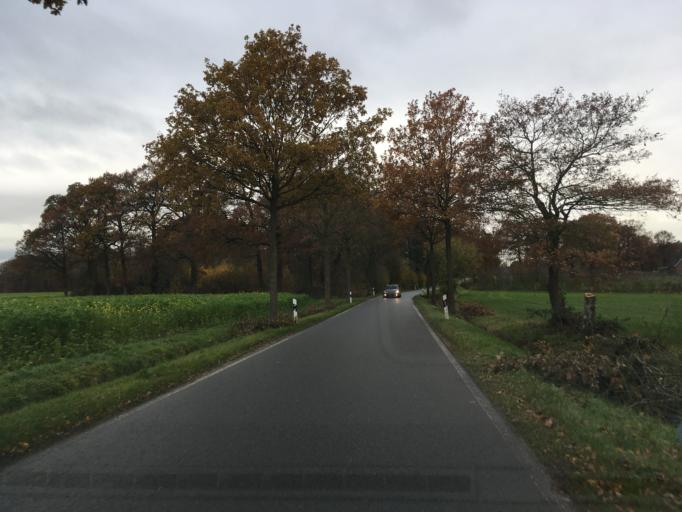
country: DE
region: North Rhine-Westphalia
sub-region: Regierungsbezirk Munster
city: Gescher
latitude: 51.9766
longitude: 7.0049
